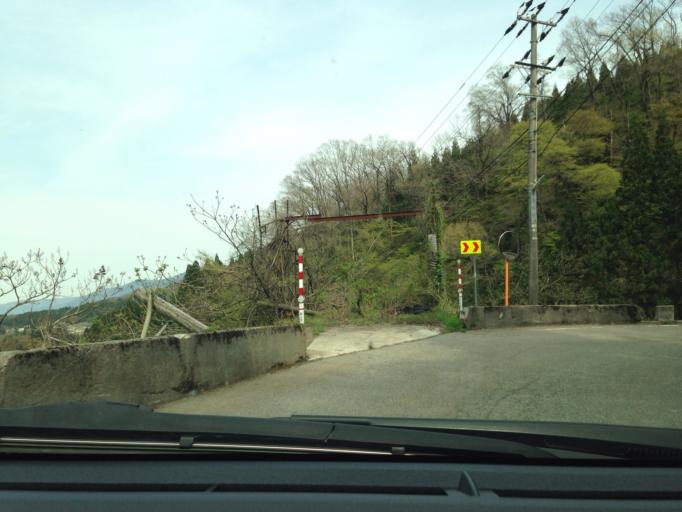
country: JP
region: Toyama
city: Fukumitsu
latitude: 36.4913
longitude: 136.8264
